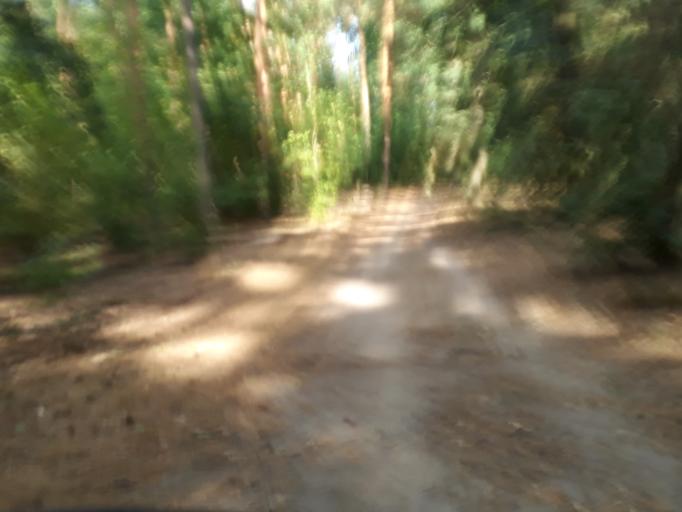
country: DE
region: Berlin
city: Grunewald
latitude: 52.4937
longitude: 13.2556
